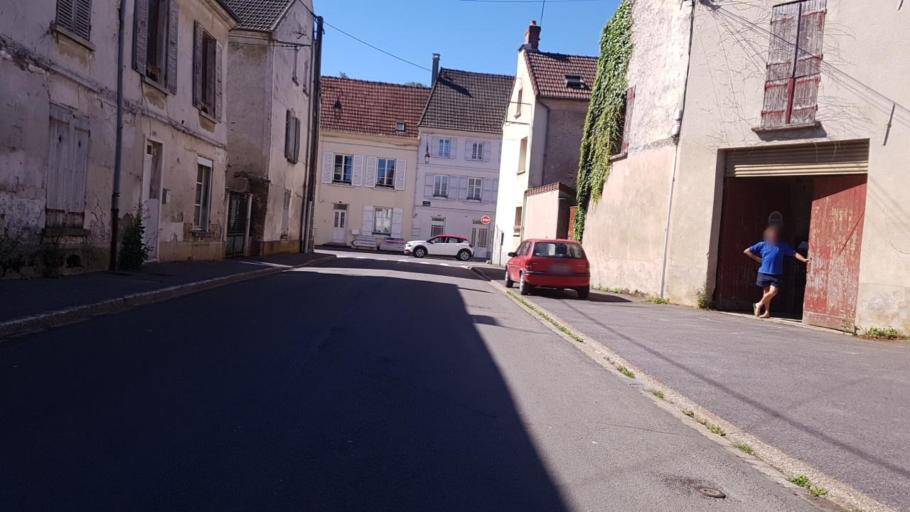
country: FR
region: Picardie
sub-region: Departement de l'Aisne
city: Charly-sur-Marne
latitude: 48.9771
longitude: 3.2826
